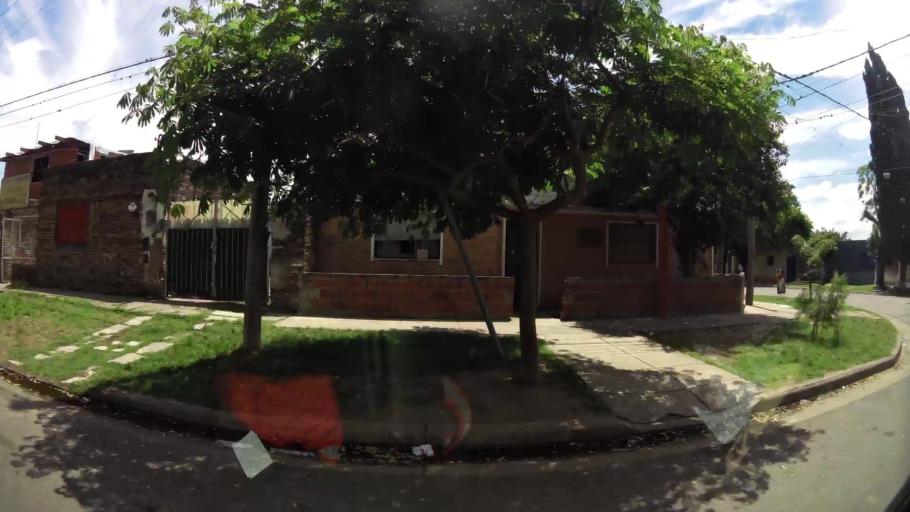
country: AR
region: Santa Fe
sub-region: Departamento de Rosario
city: Rosario
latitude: -32.9745
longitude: -60.6251
